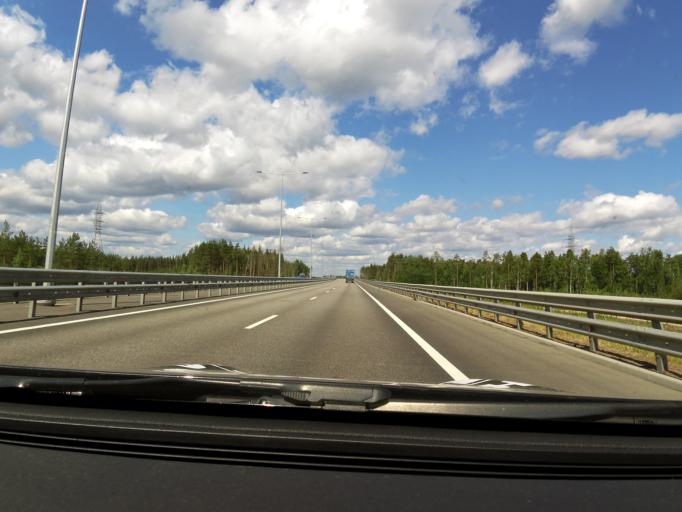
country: RU
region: Tverskaya
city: Vyshniy Volochek
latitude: 57.4107
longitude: 34.5200
